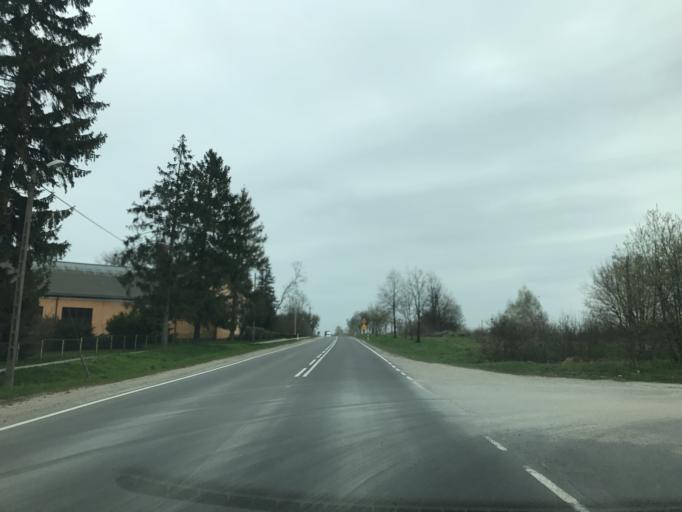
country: PL
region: Warmian-Masurian Voivodeship
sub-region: Powiat olsztynski
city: Olsztynek
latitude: 53.5885
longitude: 20.2919
